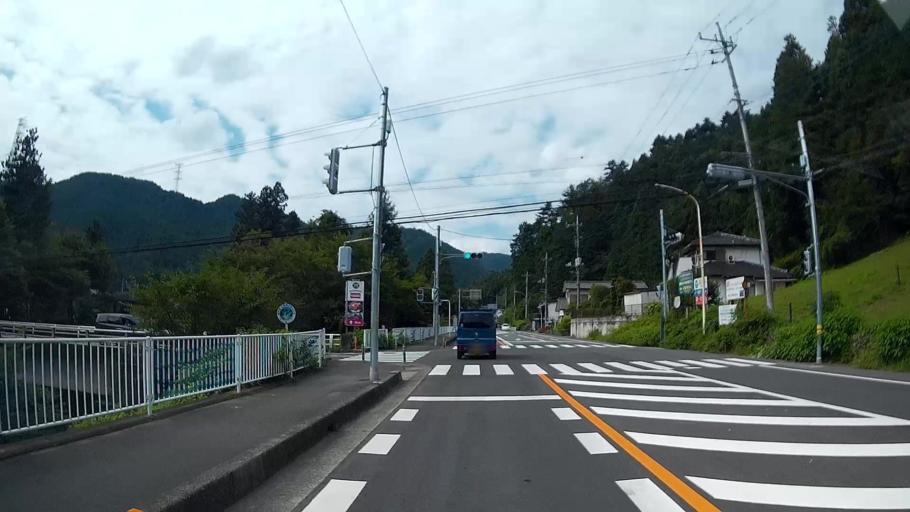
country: JP
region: Tokyo
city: Ome
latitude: 35.8638
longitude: 139.2350
